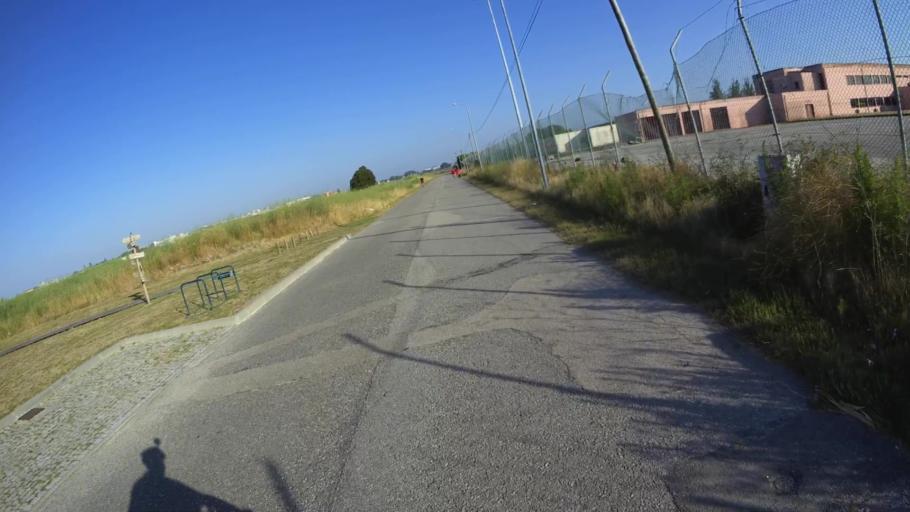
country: PT
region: Aveiro
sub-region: Aveiro
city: Aveiro
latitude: 40.6389
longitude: -8.6712
